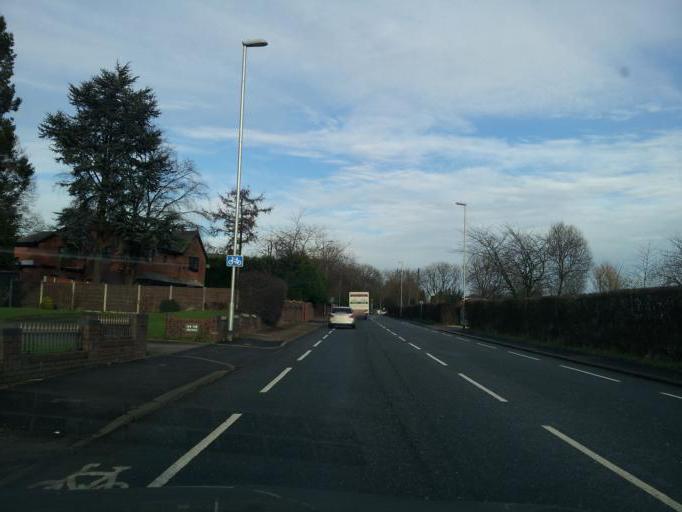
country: GB
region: England
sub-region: Manchester
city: Heywood
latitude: 53.5786
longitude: -2.2154
